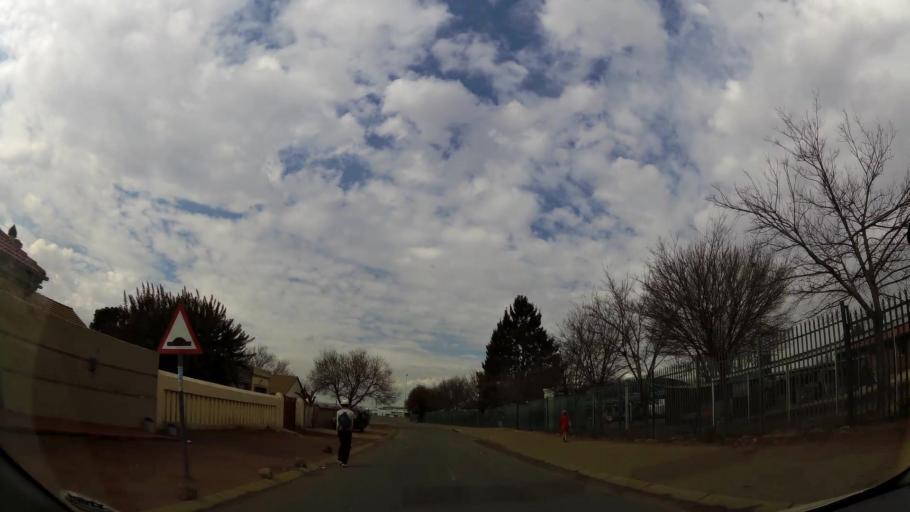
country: ZA
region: Gauteng
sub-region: Ekurhuleni Metropolitan Municipality
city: Germiston
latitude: -26.3883
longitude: 28.1605
